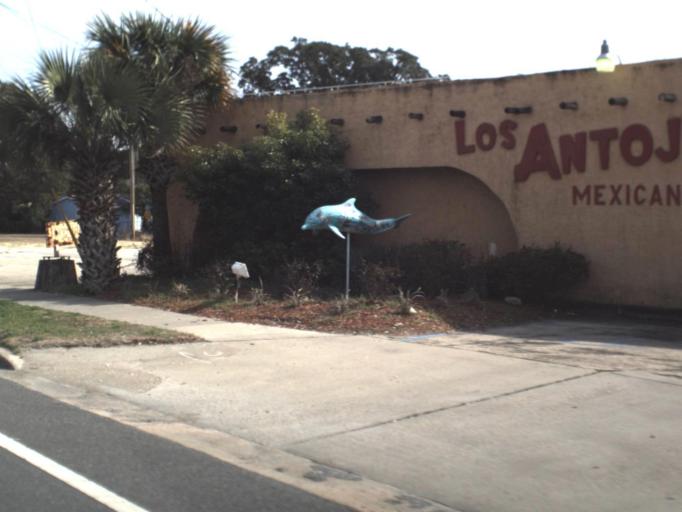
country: US
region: Florida
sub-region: Bay County
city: Upper Grand Lagoon
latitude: 30.1814
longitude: -85.7229
